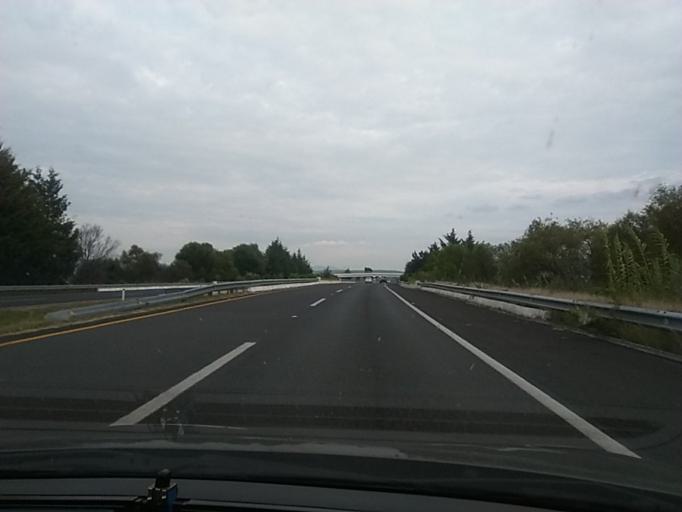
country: MX
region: Michoacan
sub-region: Jimenez
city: Copandaro (Copandaro del Cuatro)
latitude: 19.9358
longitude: -101.6166
